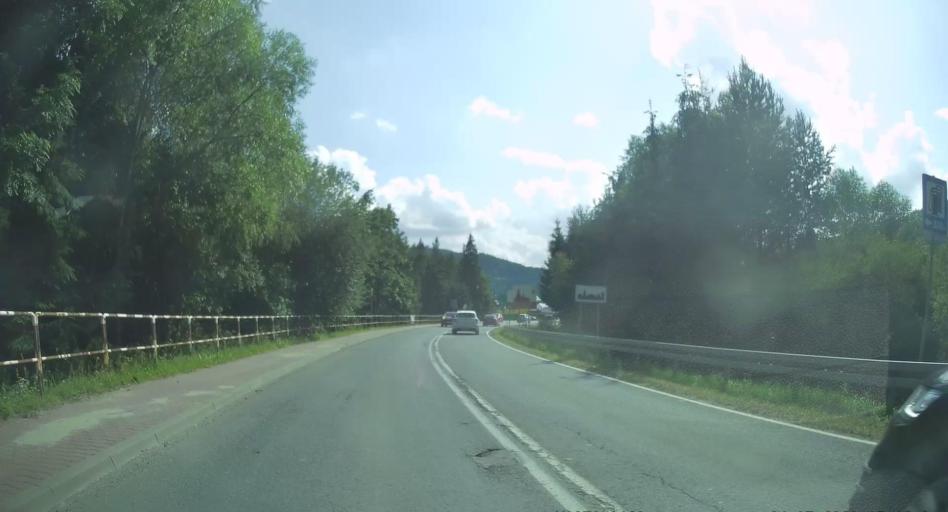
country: PL
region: Lesser Poland Voivodeship
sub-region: Powiat nowosadecki
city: Krynica-Zdroj
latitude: 49.3719
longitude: 20.9496
